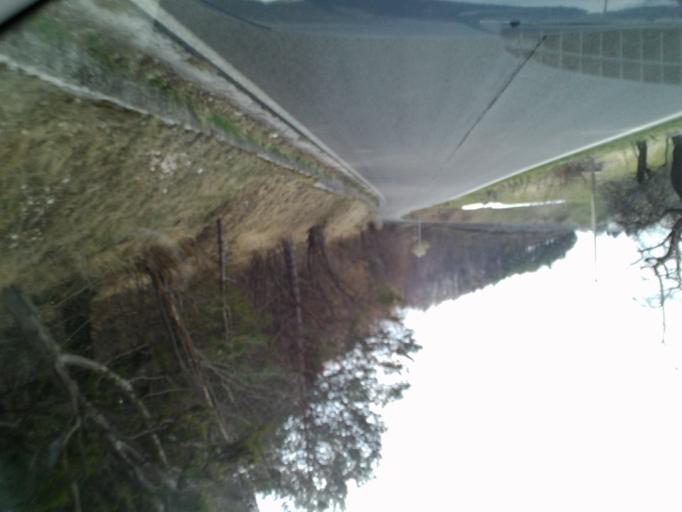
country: IT
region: Veneto
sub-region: Provincia di Verona
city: Sant'Anna d'Alfaedo
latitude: 45.6326
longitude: 10.9481
